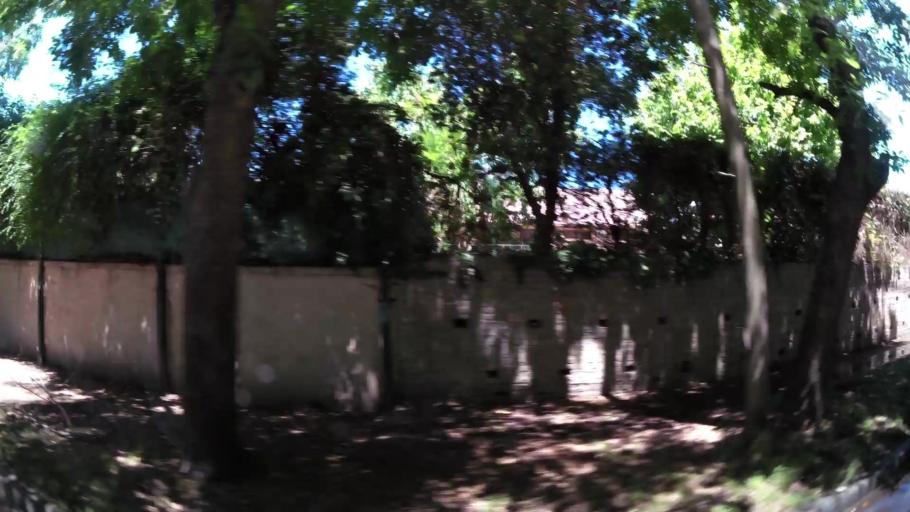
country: AR
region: Buenos Aires
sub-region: Partido de San Isidro
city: San Isidro
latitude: -34.4548
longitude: -58.5145
